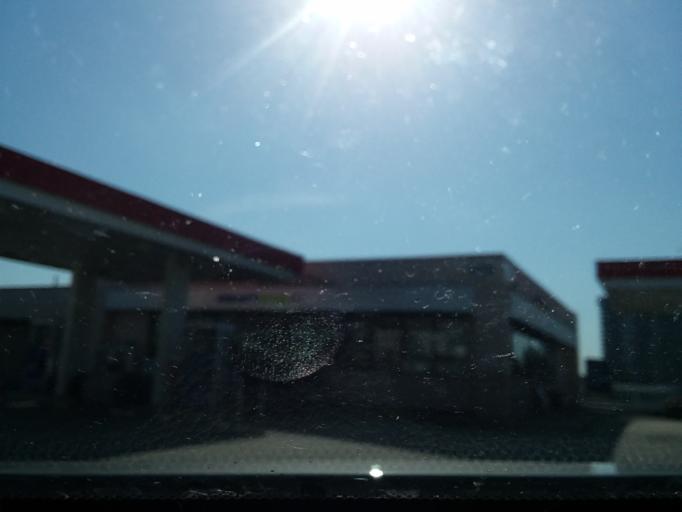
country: CA
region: British Columbia
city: New Westminster
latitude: 49.2488
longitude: -122.8932
